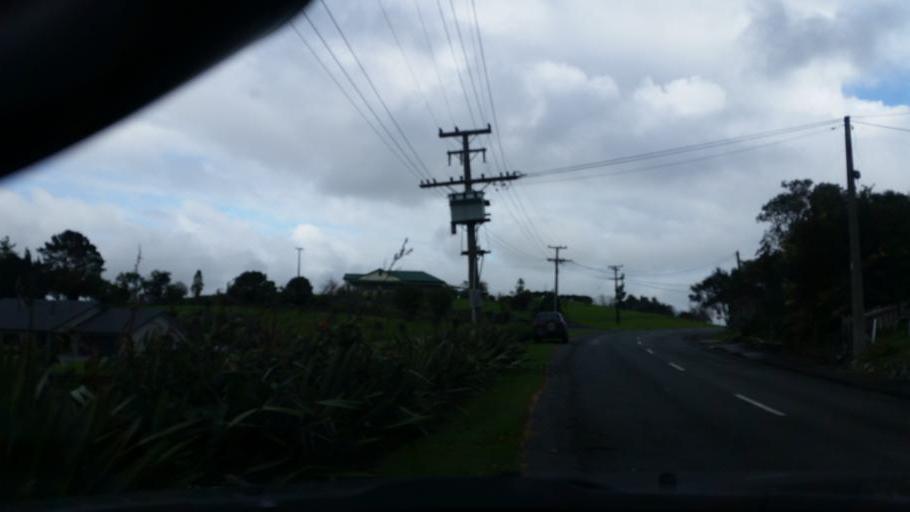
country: NZ
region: Northland
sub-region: Whangarei
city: Ruakaka
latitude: -36.1166
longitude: 174.3497
